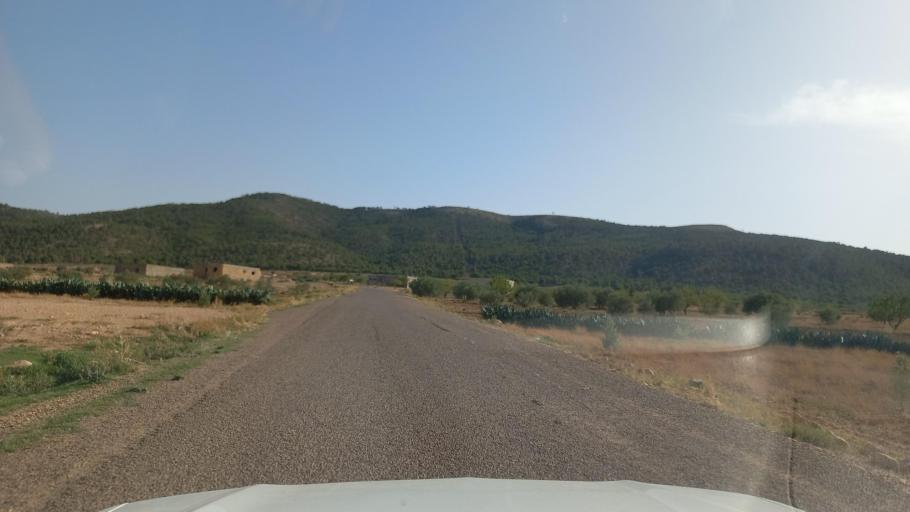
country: TN
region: Al Qasrayn
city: Kasserine
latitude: 35.3414
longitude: 8.8347
